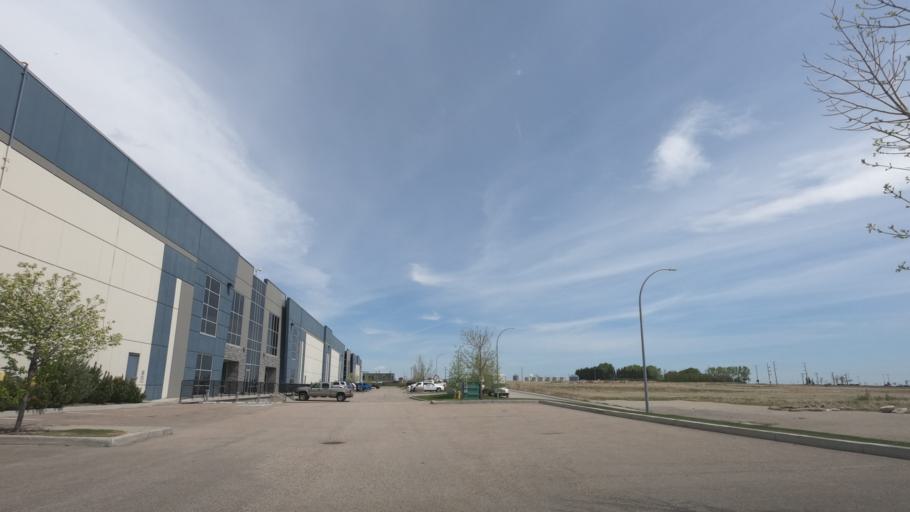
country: CA
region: Alberta
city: Airdrie
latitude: 51.3029
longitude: -113.9840
